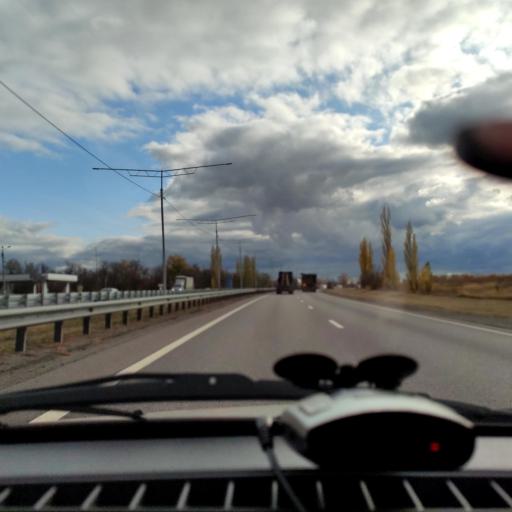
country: RU
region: Voronezj
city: Ramon'
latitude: 51.9747
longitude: 39.2215
